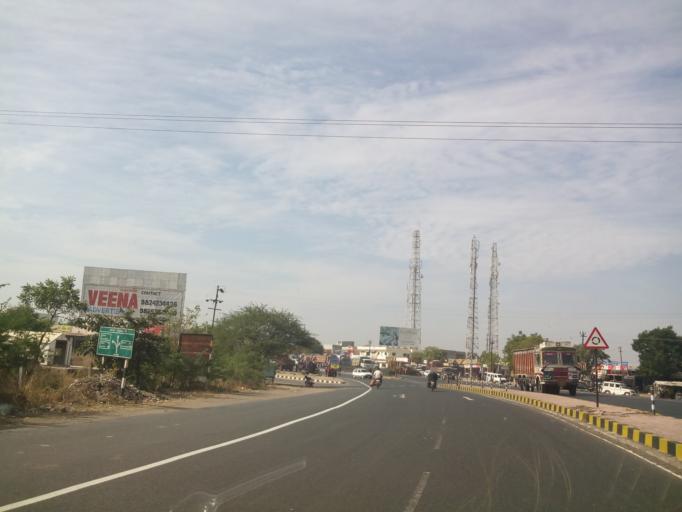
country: IN
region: Gujarat
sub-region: Rajkot
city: Rajkot
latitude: 22.3603
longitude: 70.9393
